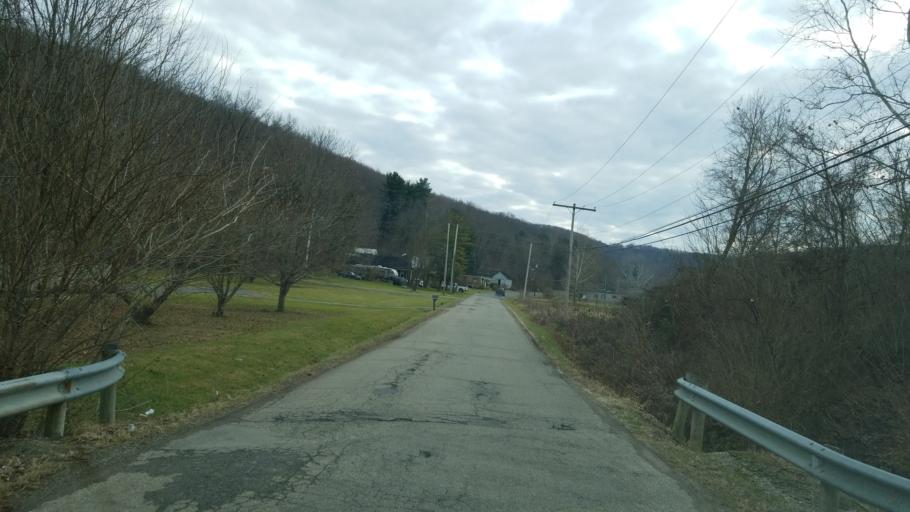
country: US
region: Ohio
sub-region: Highland County
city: Greenfield
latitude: 39.2223
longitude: -83.2690
